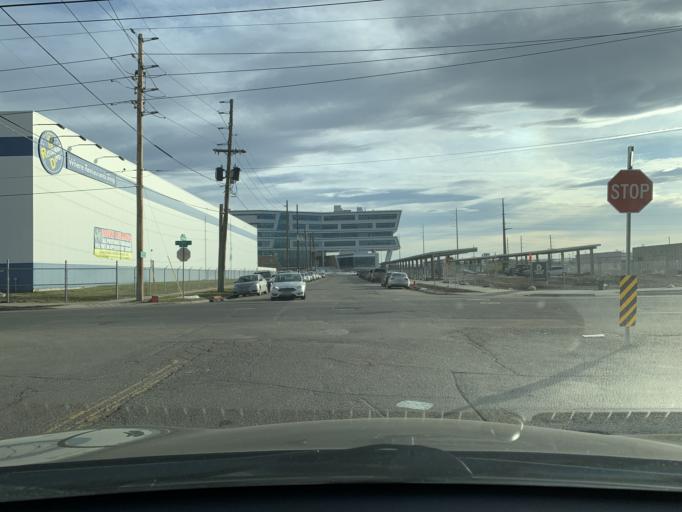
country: US
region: Colorado
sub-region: Denver County
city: Denver
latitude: 39.7370
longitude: -105.0104
